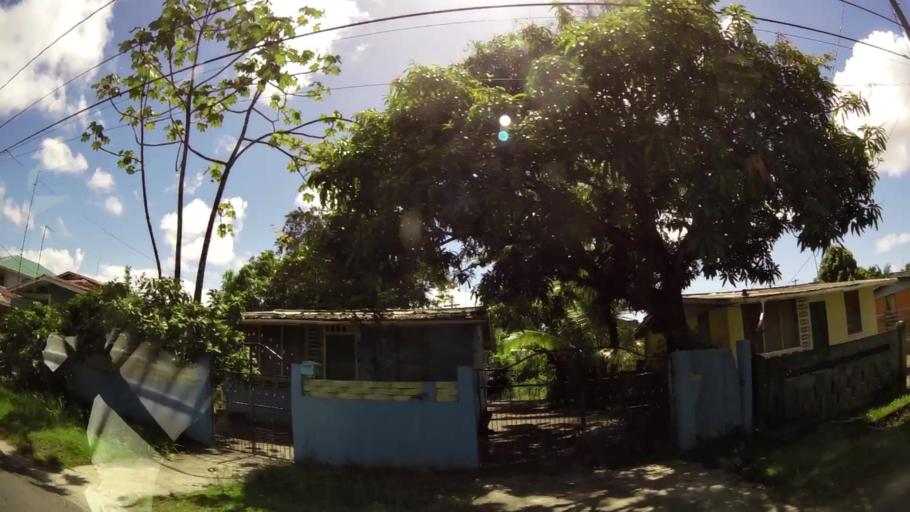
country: GY
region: Demerara-Mahaica
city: Georgetown
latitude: 6.7946
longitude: -58.1386
